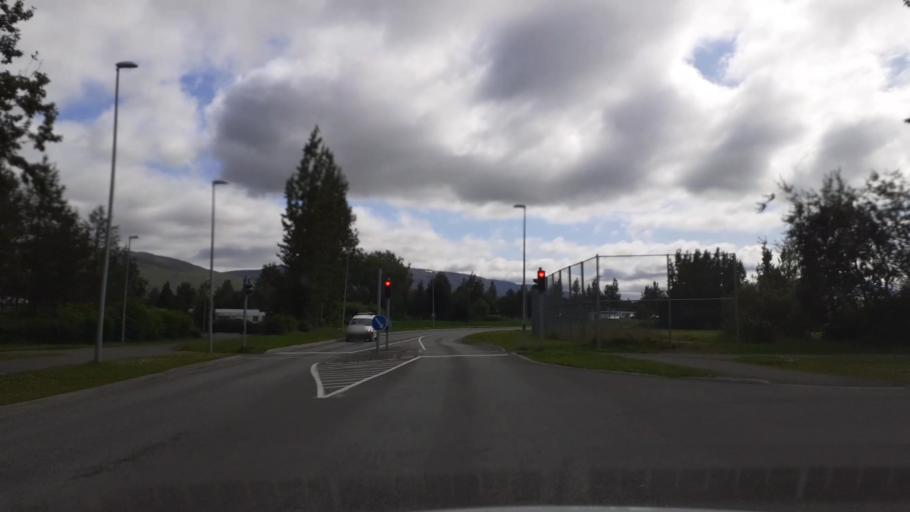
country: IS
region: Northeast
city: Akureyri
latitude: 65.6768
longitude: -18.1123
